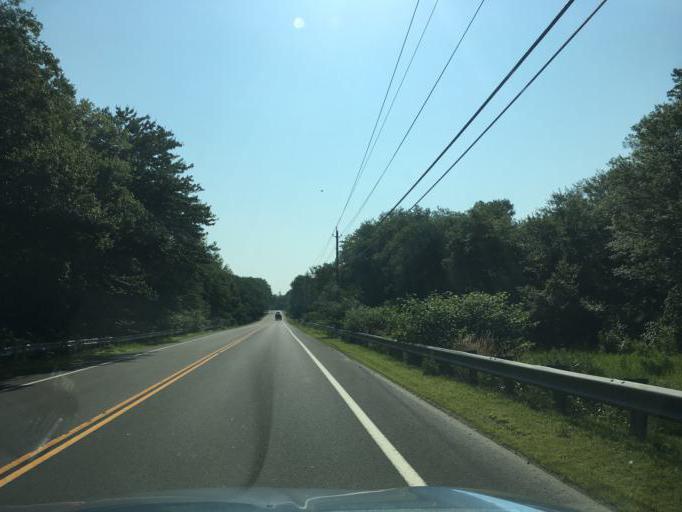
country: US
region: Rhode Island
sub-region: Washington County
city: Kingston
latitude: 41.4918
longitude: -71.4803
